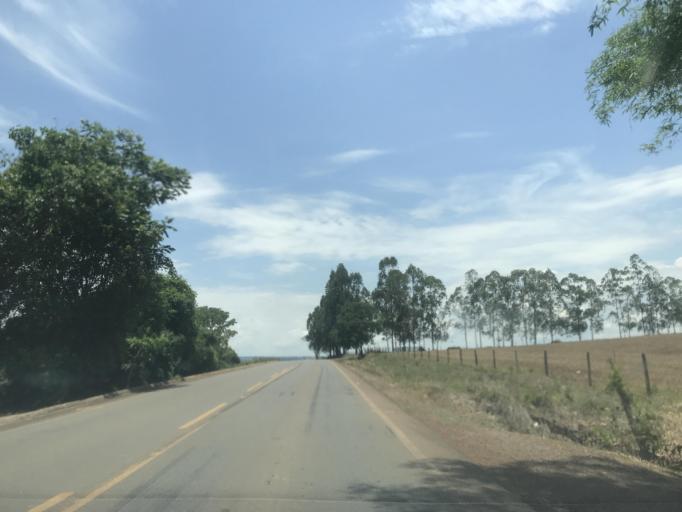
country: BR
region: Goias
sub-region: Vianopolis
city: Vianopolis
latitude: -16.6296
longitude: -48.3552
